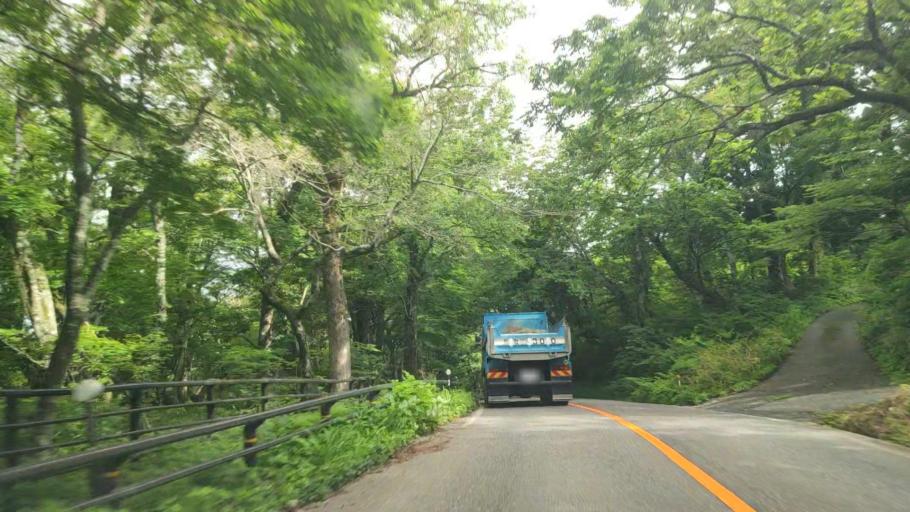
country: JP
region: Tottori
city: Yonago
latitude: 35.3892
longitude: 133.5284
